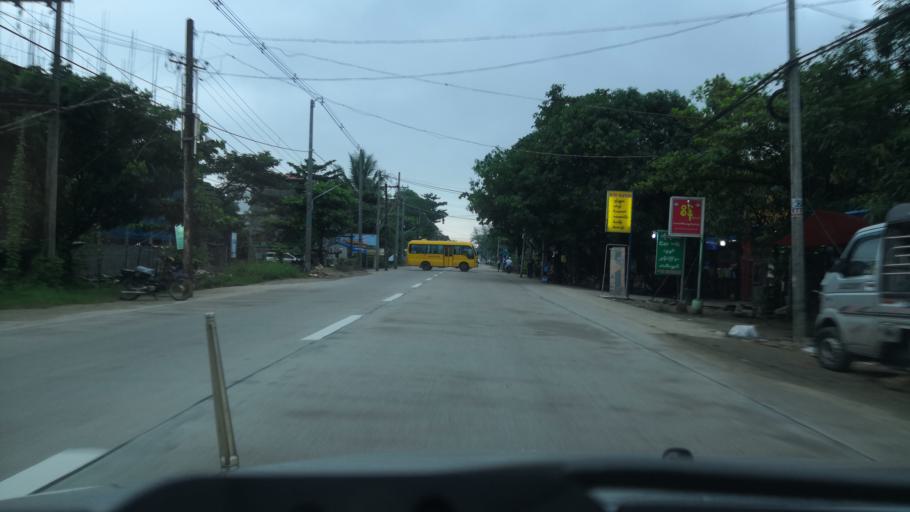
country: MM
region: Yangon
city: Yangon
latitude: 16.8816
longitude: 96.1696
